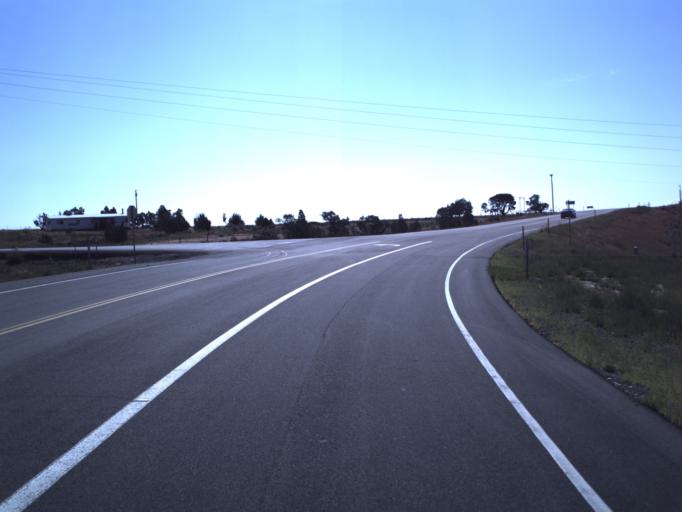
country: US
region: Utah
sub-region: Duchesne County
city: Duchesne
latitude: 40.3583
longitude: -110.3888
